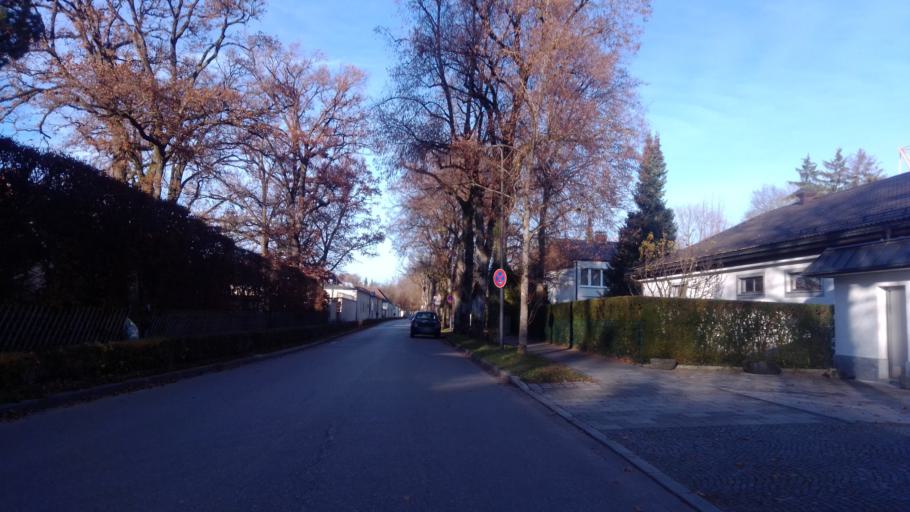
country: DE
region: Bavaria
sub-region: Upper Bavaria
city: Pullach im Isartal
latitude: 48.0589
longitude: 11.5264
